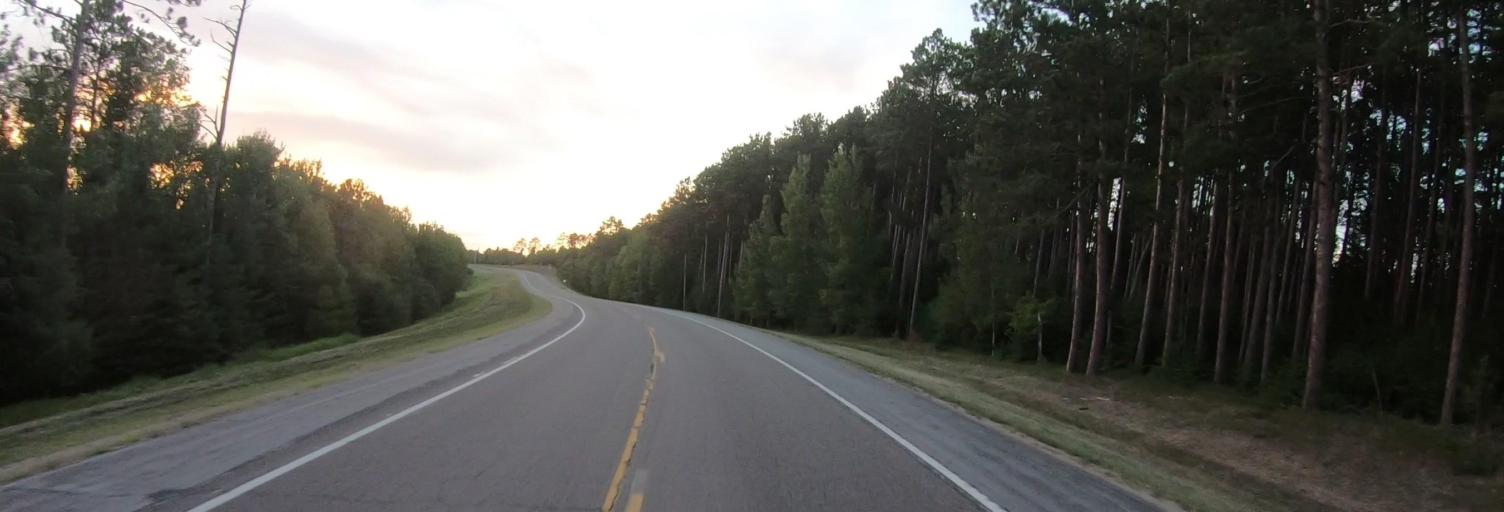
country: US
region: Minnesota
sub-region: Saint Louis County
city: Aurora
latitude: 47.8408
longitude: -92.3733
